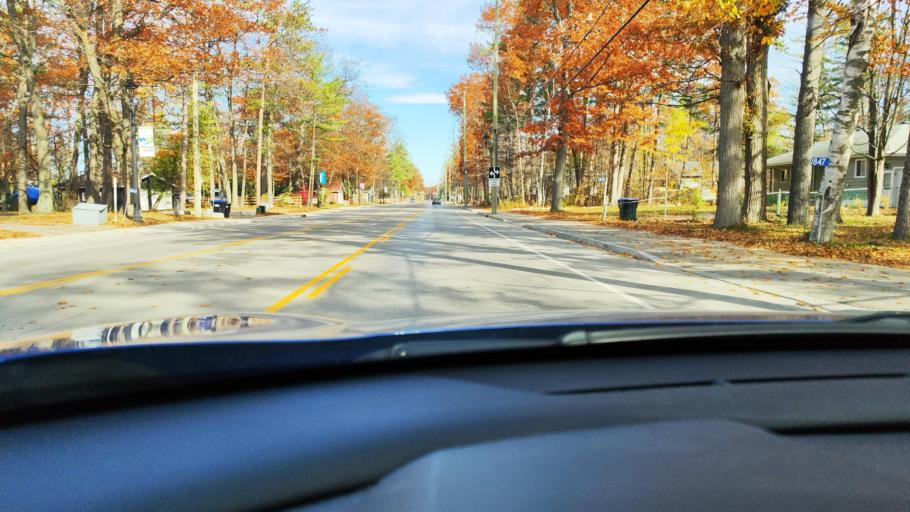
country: CA
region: Ontario
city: Wasaga Beach
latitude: 44.4977
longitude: -80.0402
